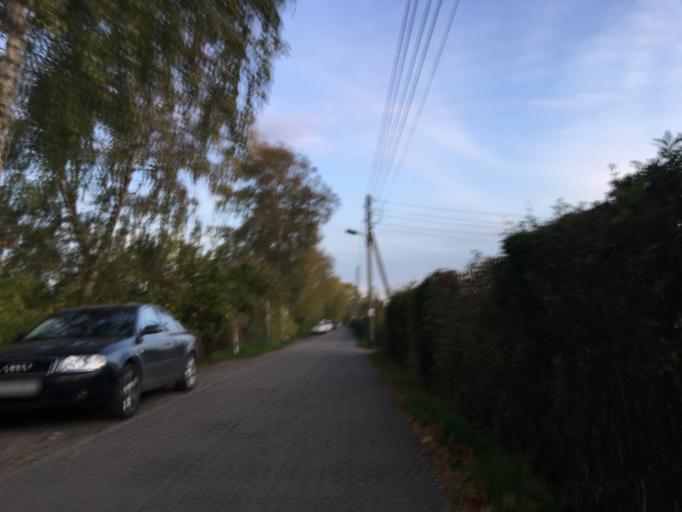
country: DE
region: Berlin
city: Buchholz
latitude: 52.6143
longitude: 13.4134
